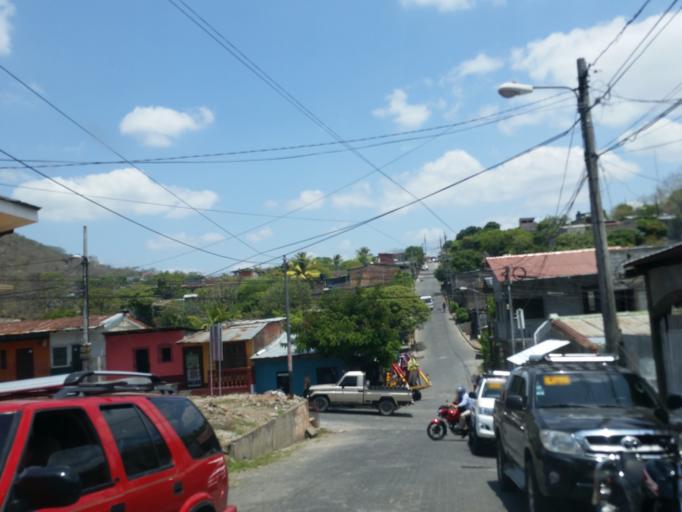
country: NI
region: Boaco
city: Boaco
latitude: 12.4728
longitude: -85.6572
